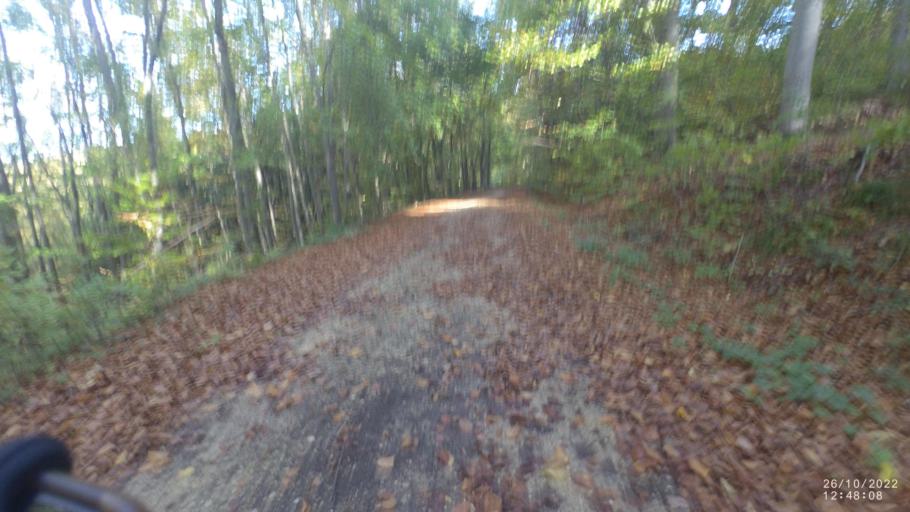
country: DE
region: Baden-Wuerttemberg
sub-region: Regierungsbezirk Stuttgart
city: Eschenbach
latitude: 48.6456
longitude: 9.6867
